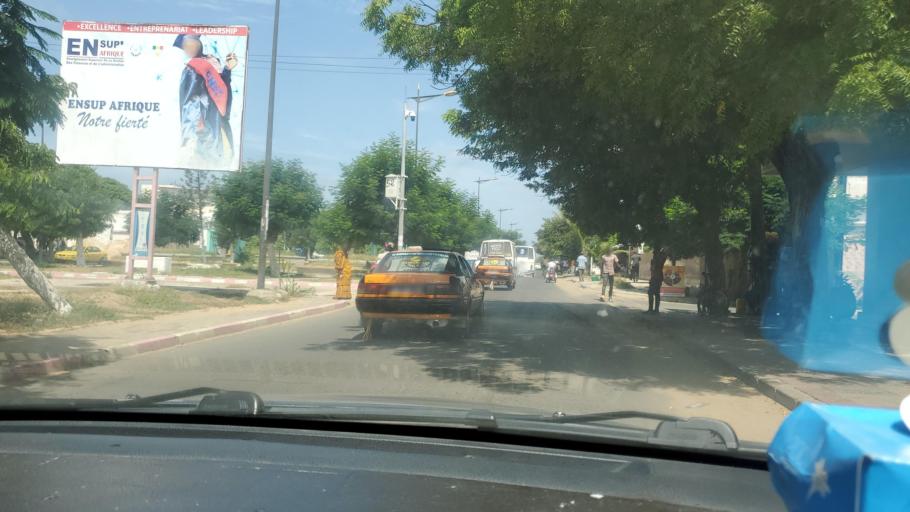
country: SN
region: Dakar
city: Grand Dakar
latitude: 14.7158
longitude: -17.4554
